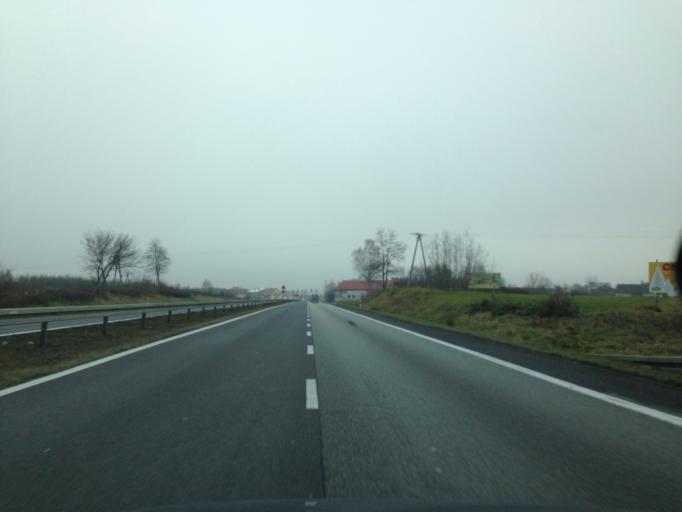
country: PL
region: Silesian Voivodeship
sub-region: Powiat czestochowski
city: Kamienica Polska
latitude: 50.6325
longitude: 19.1369
